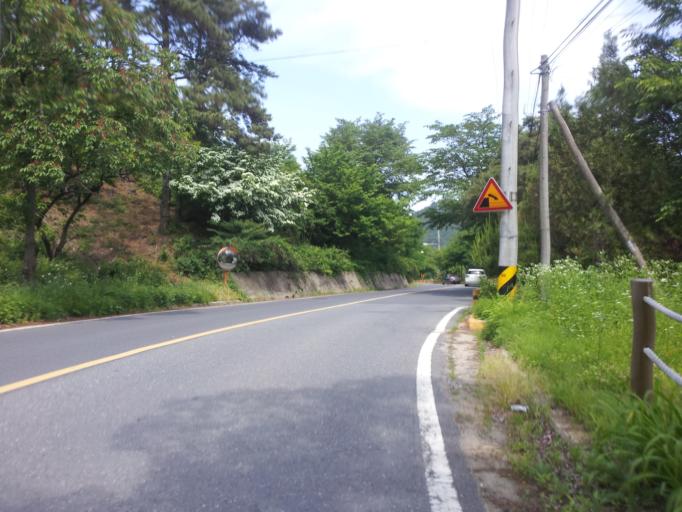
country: KR
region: Daejeon
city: Sintansin
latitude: 36.4282
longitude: 127.4666
